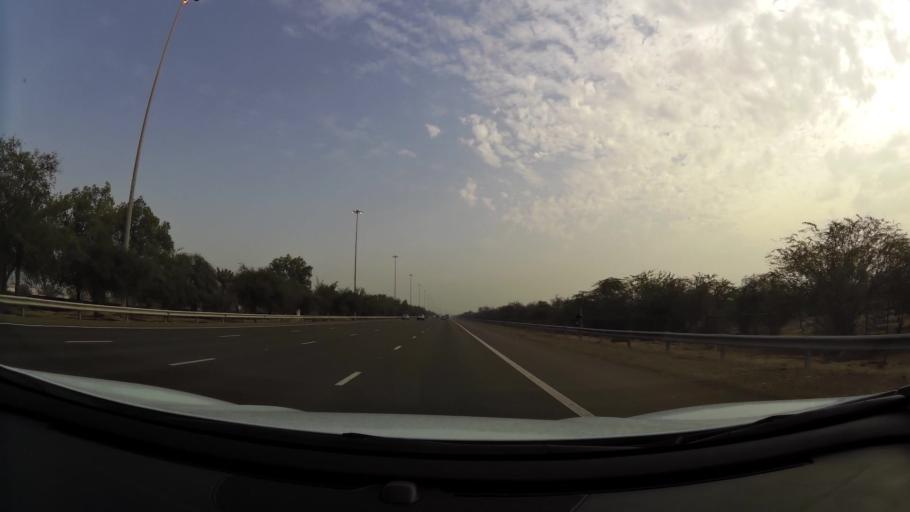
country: AE
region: Abu Dhabi
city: Abu Dhabi
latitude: 24.6351
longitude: 54.7297
